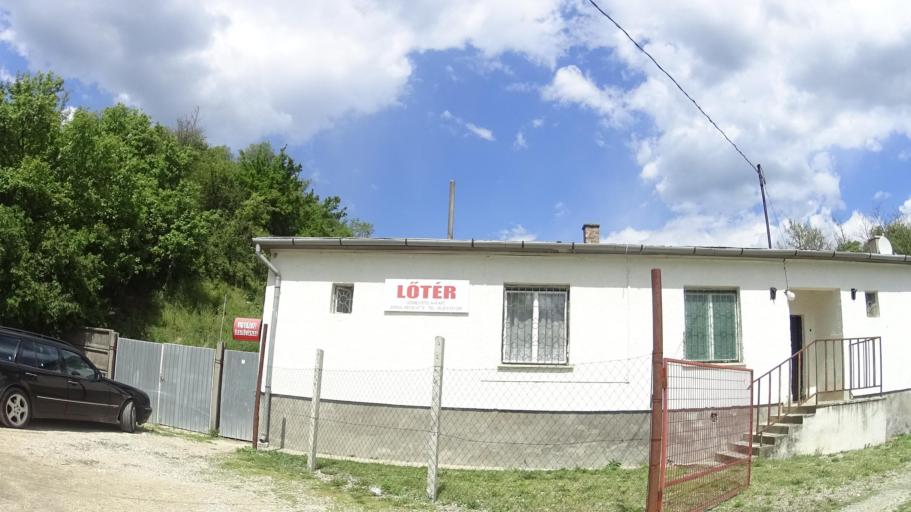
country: HU
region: Komarom-Esztergom
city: Dorog
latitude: 47.7181
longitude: 18.7512
